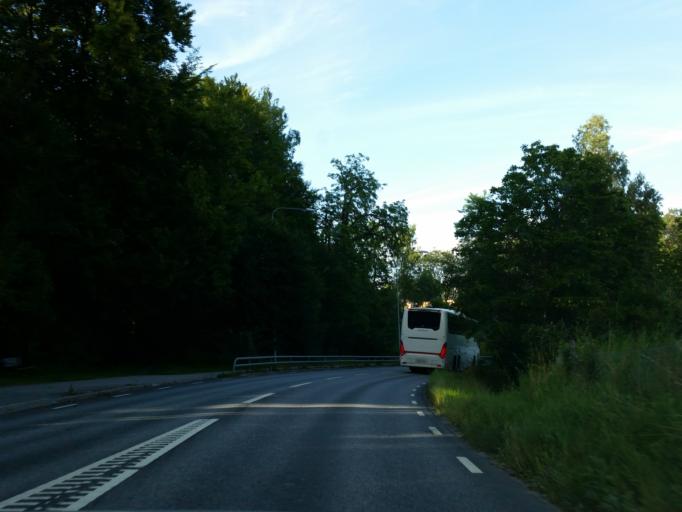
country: SE
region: Stockholm
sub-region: Sodertalje Kommun
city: Molnbo
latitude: 59.0492
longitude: 17.4212
